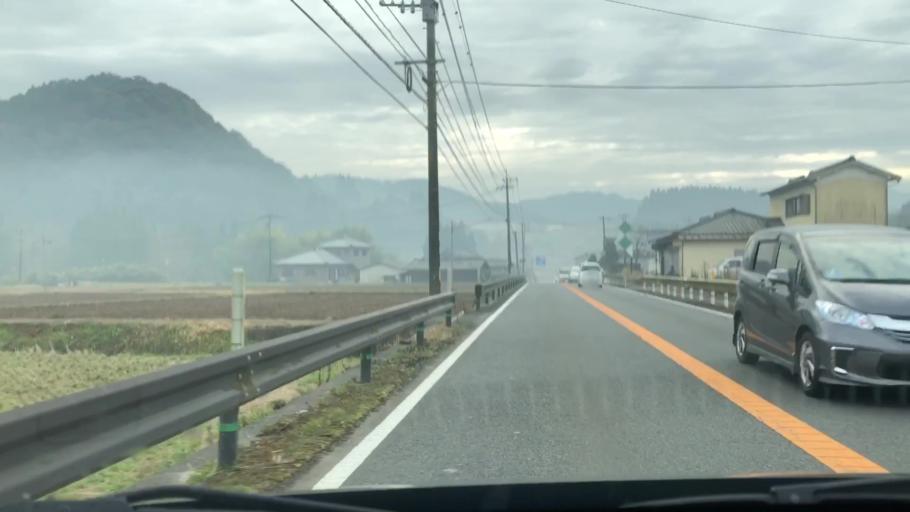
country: JP
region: Oita
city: Usuki
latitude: 33.0192
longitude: 131.6991
